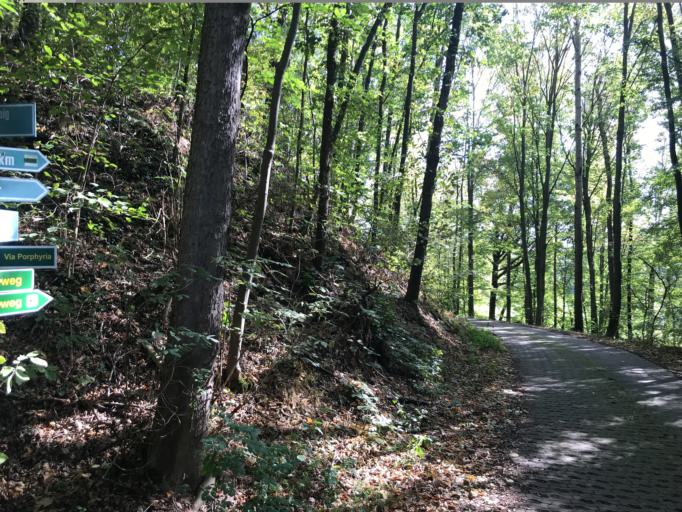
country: DE
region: Saxony
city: Seelitz
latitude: 51.0287
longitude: 12.8238
